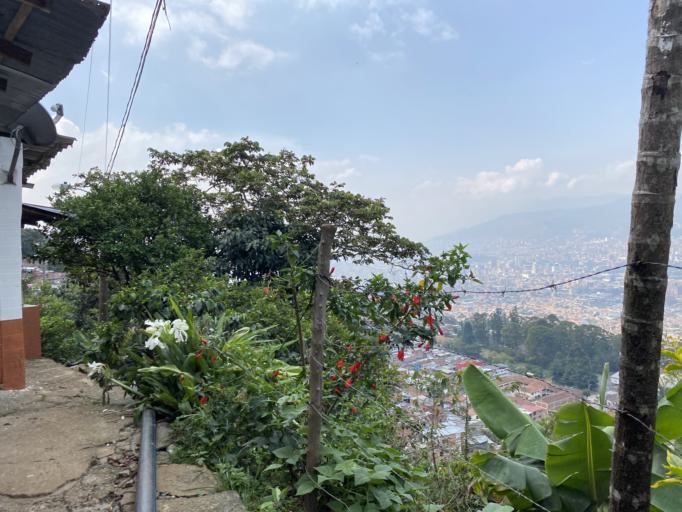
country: CO
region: Antioquia
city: Medellin
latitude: 6.2791
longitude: -75.5438
